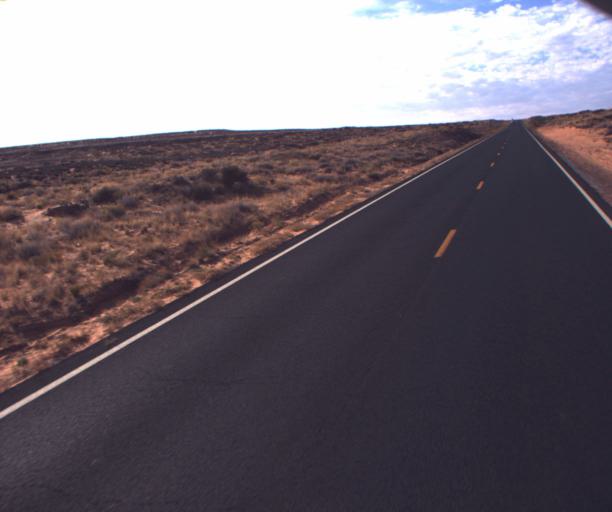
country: US
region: Arizona
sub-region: Apache County
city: Many Farms
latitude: 36.9008
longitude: -109.6253
